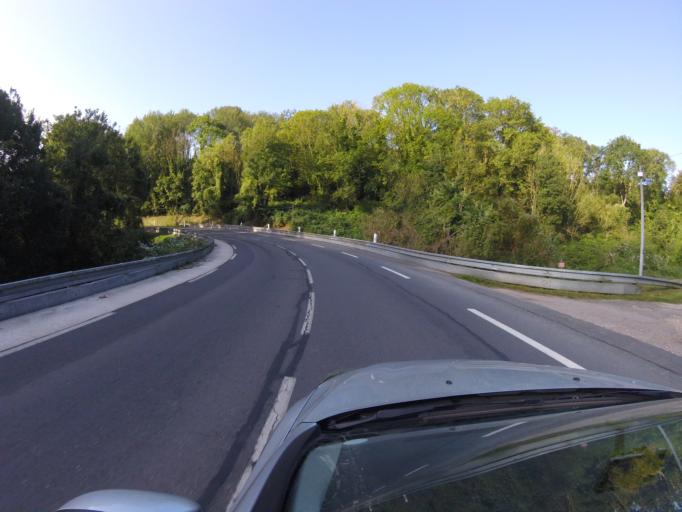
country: FR
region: Haute-Normandie
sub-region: Departement de la Seine-Maritime
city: Fecamp
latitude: 49.7630
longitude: 0.3952
